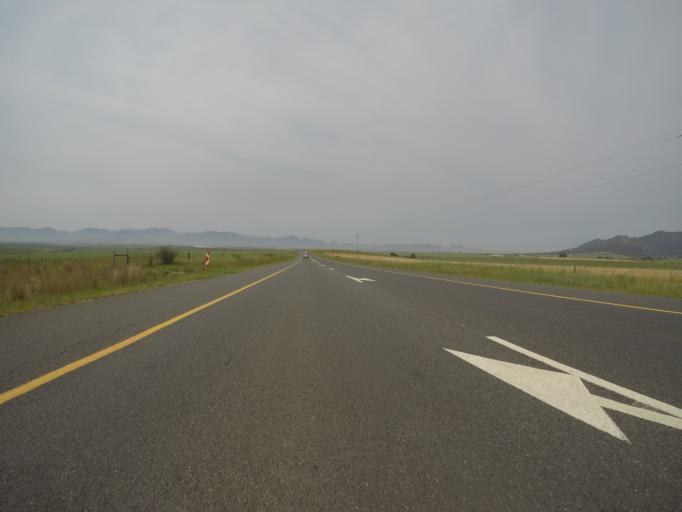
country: ZA
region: Western Cape
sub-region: West Coast District Municipality
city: Malmesbury
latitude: -33.5408
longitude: 18.8589
